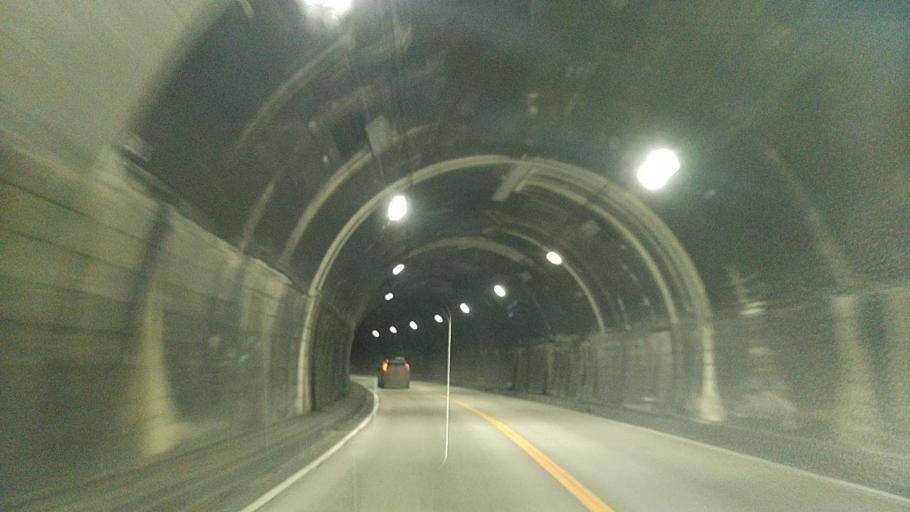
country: JP
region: Osaka
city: Ikeda
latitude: 34.9009
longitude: 135.4092
